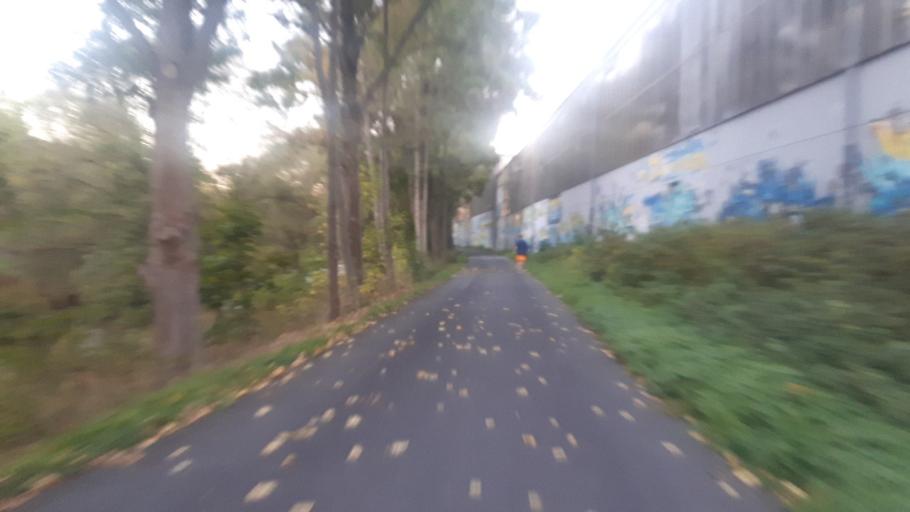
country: DE
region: North Rhine-Westphalia
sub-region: Regierungsbezirk Arnsberg
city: Siegen
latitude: 50.8576
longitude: 8.0076
